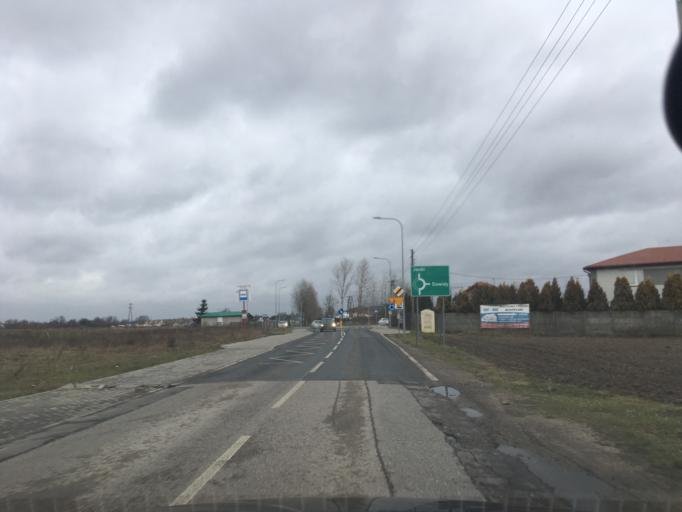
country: PL
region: Masovian Voivodeship
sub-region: Powiat piaseczynski
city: Lesznowola
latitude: 52.1215
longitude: 20.9300
